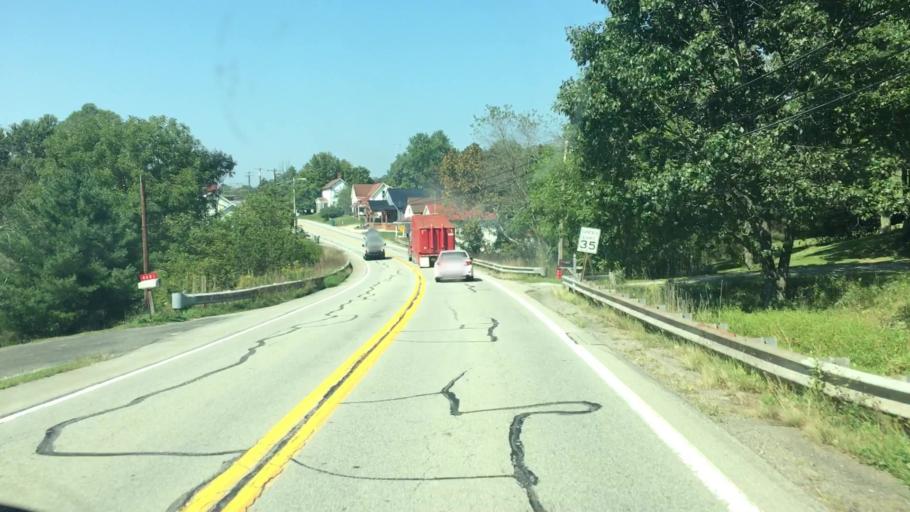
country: US
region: Pennsylvania
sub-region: Washington County
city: Washington
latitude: 40.0445
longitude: -80.2892
